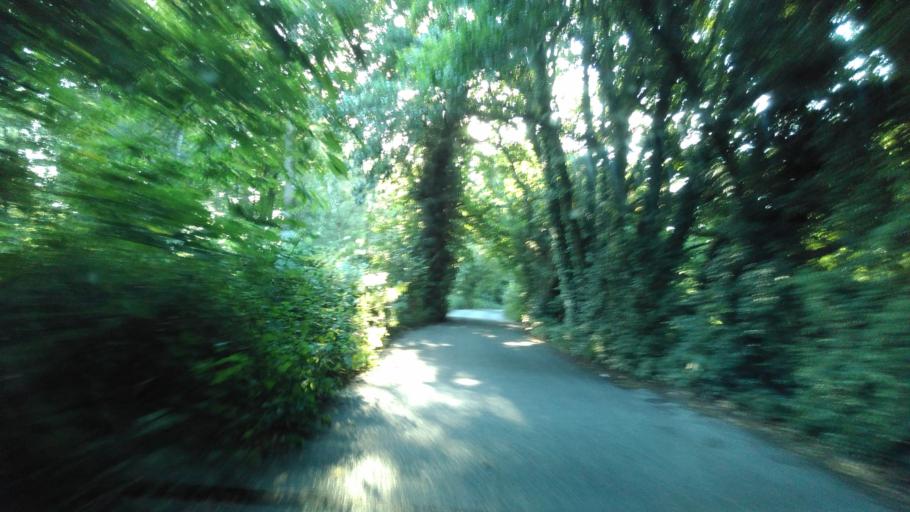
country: GB
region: England
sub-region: Kent
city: Chartham
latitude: 51.2774
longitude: 1.0307
